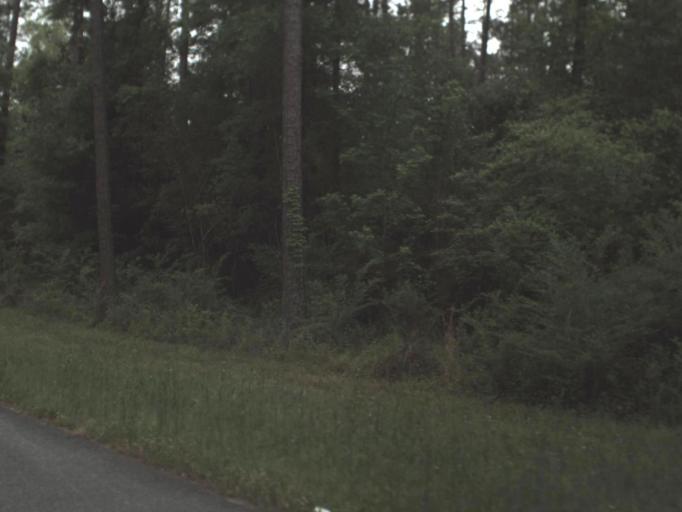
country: US
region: Florida
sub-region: Santa Rosa County
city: Point Baker
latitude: 30.7968
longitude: -87.0413
